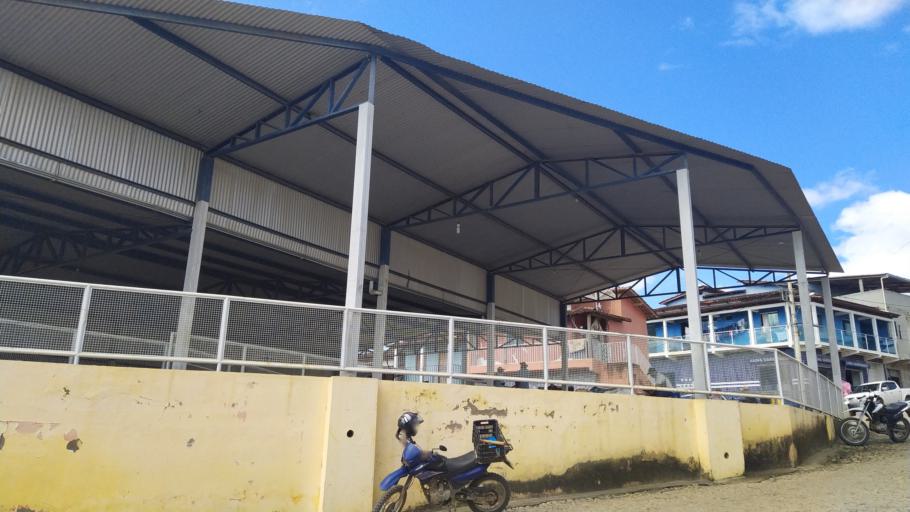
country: BR
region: Bahia
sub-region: Itanhem
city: Itanhem
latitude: -16.7342
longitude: -40.4205
